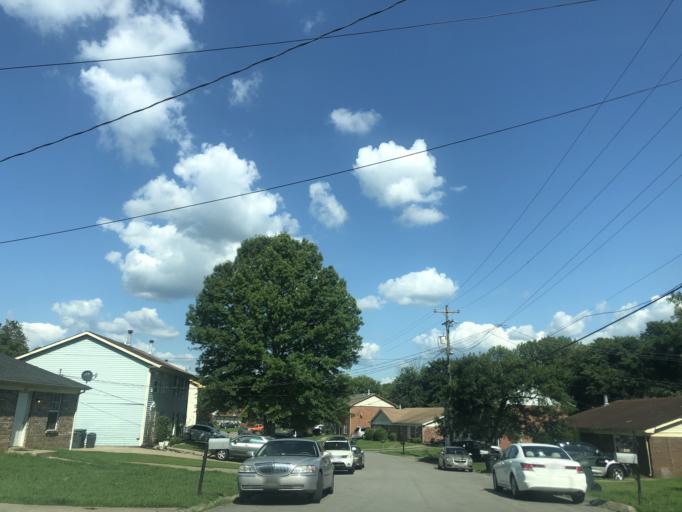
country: US
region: Tennessee
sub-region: Davidson County
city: Lakewood
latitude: 36.1977
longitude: -86.6021
